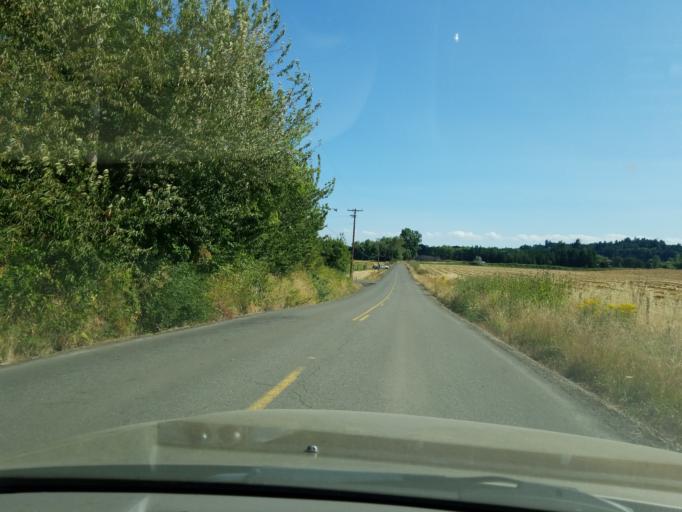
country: US
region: Oregon
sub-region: Yamhill County
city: McMinnville
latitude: 45.2354
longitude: -123.2309
